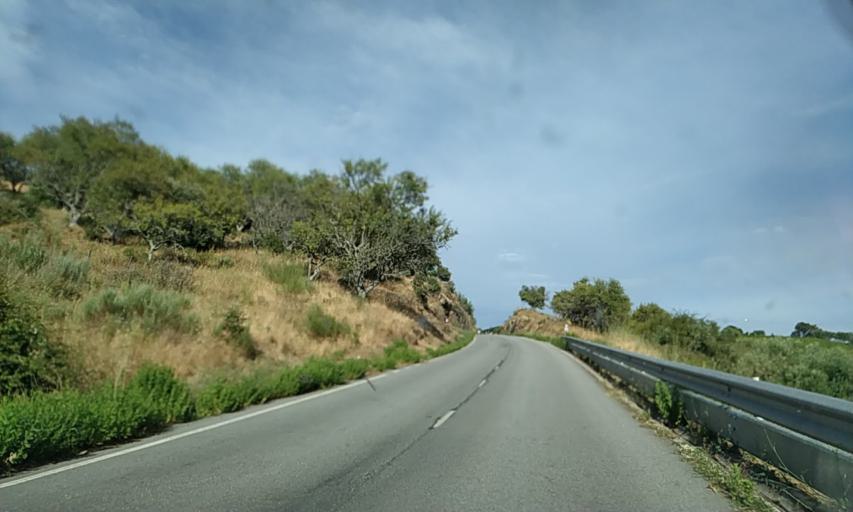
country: PT
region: Viseu
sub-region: Sao Joao da Pesqueira
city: Sao Joao da Pesqueira
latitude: 41.1426
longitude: -7.4287
